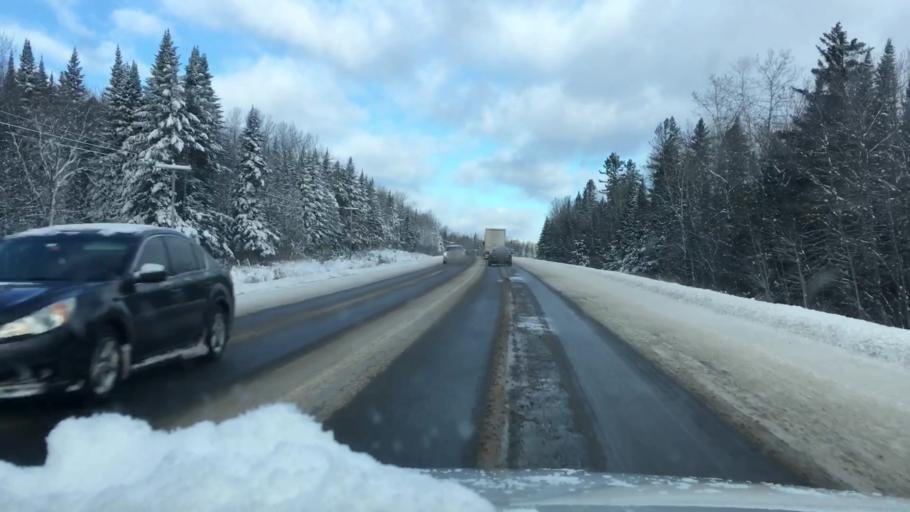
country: US
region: Maine
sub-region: Aroostook County
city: Caribou
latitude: 46.8351
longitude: -67.9980
